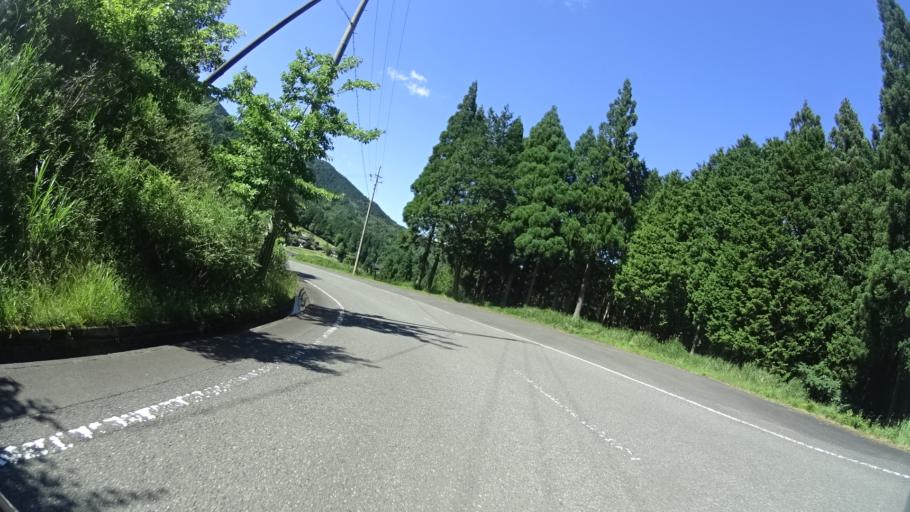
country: JP
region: Kyoto
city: Fukuchiyama
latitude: 35.3985
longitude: 135.0777
